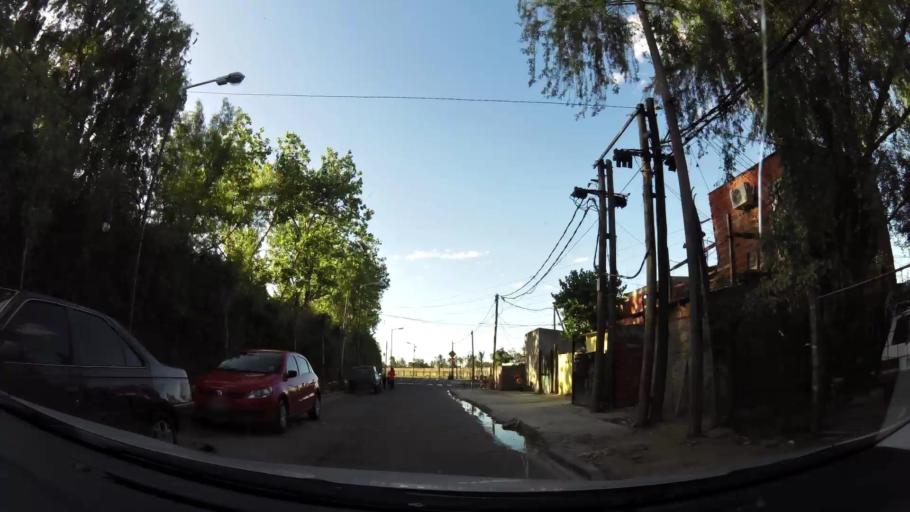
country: AR
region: Buenos Aires
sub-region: Partido de Tigre
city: Tigre
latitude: -34.4600
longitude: -58.5534
